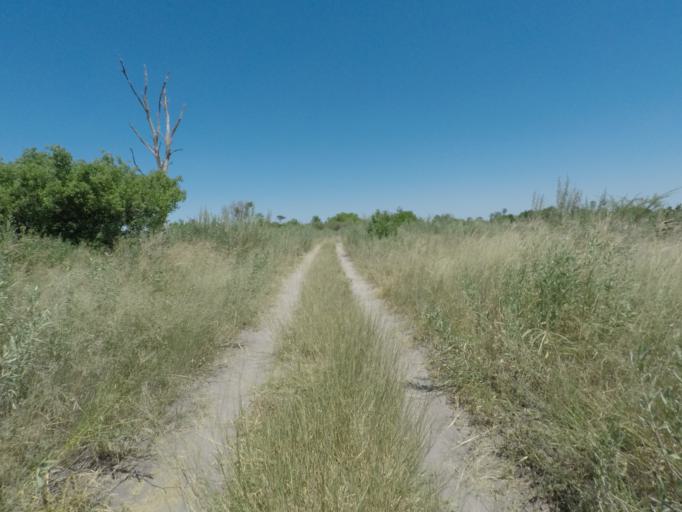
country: BW
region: North West
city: Maun
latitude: -19.4742
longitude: 23.5532
